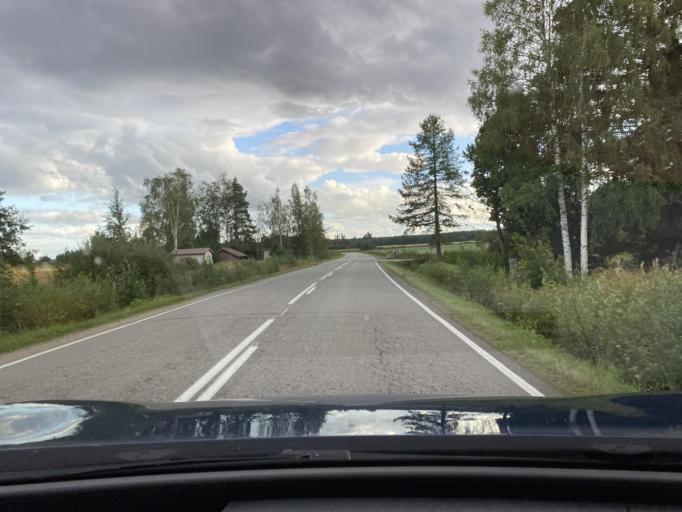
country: FI
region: Satakunta
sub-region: Pohjois-Satakunta
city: Karvia
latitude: 62.3443
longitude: 22.7120
